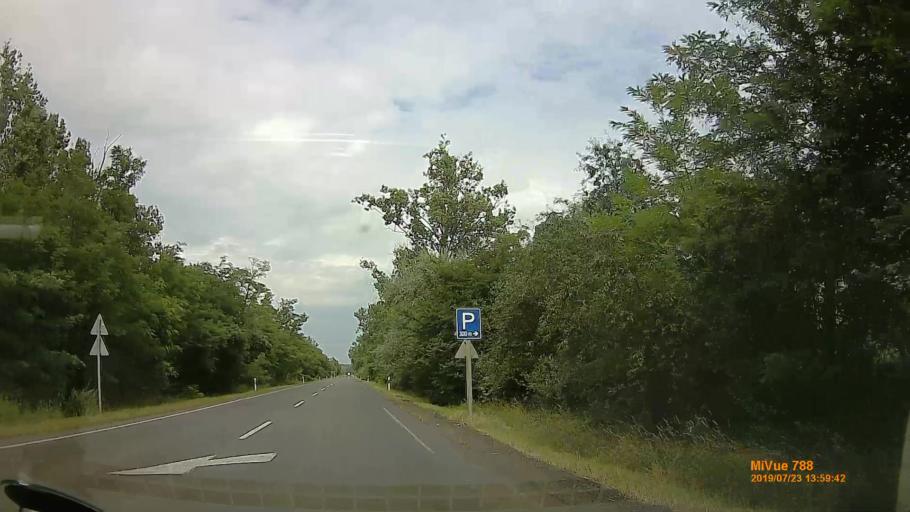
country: HU
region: Szabolcs-Szatmar-Bereg
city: Tiszavasvari
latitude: 47.9289
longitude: 21.2971
